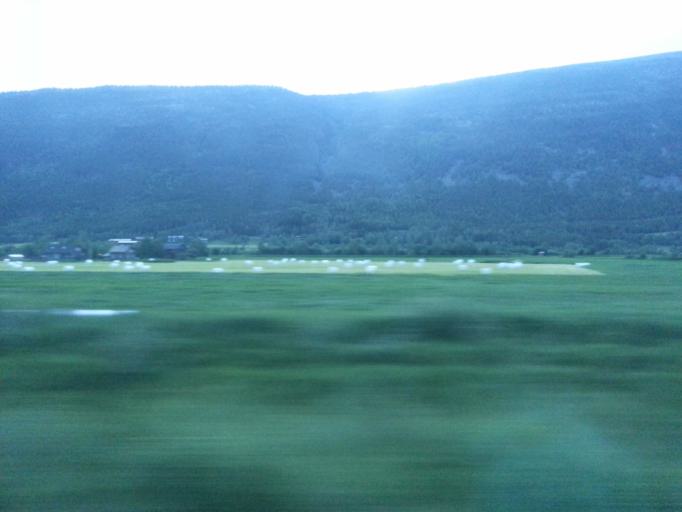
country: NO
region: Oppland
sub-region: Sel
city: Otta
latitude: 61.8253
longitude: 9.4994
